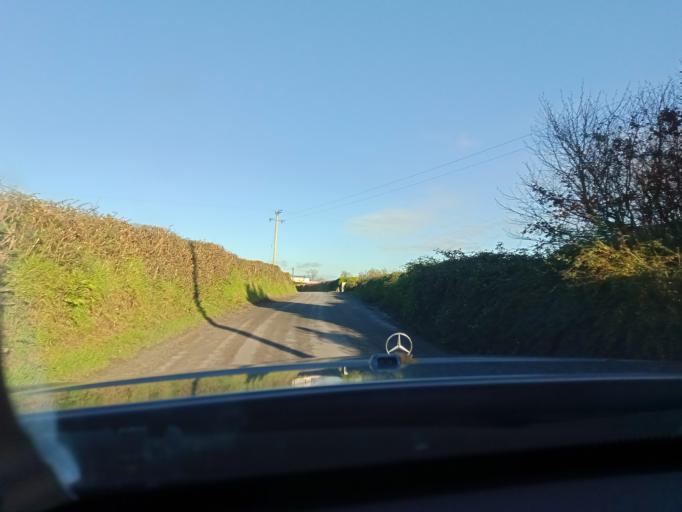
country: IE
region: Leinster
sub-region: Kilkenny
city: Mooncoin
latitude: 52.2884
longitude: -7.2335
